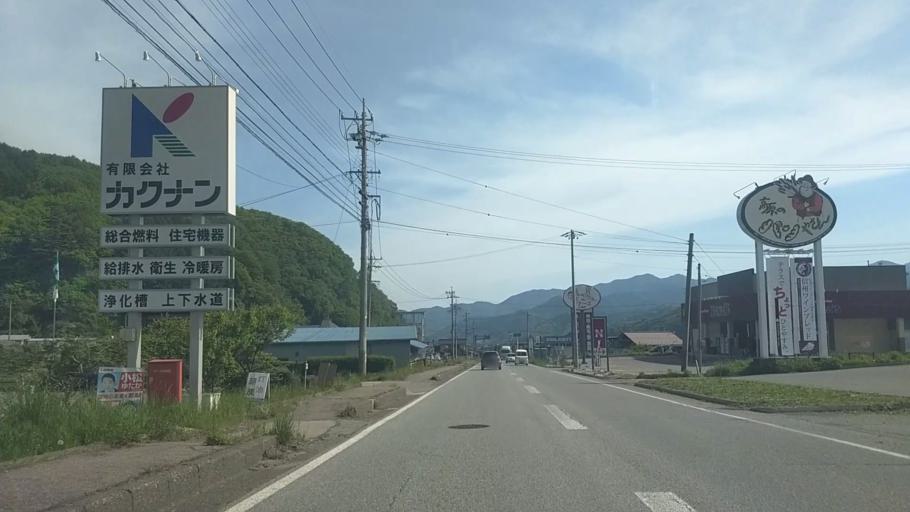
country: JP
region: Nagano
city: Saku
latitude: 36.0684
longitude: 138.4747
